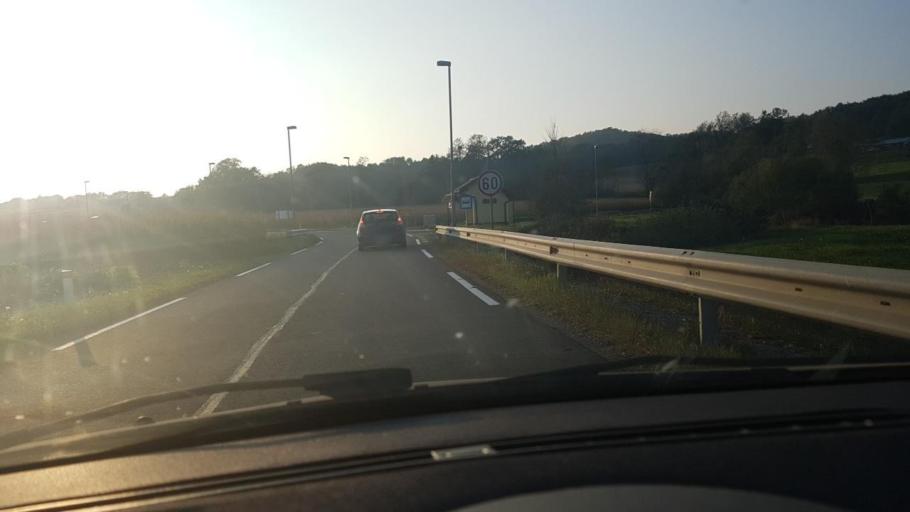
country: SI
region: Majsperk
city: Majsperk
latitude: 46.3365
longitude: 15.7054
